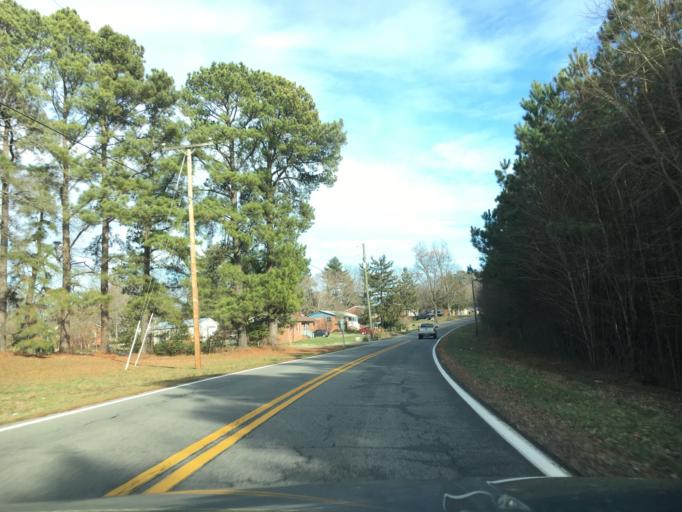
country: US
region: Virginia
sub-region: Halifax County
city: South Boston
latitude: 36.7360
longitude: -78.8853
